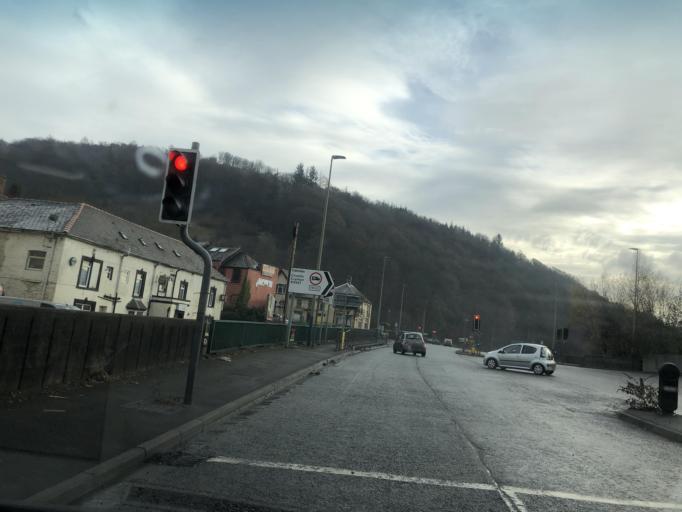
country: GB
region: Wales
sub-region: Caerphilly County Borough
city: Crumlin
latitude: 51.6800
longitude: -3.1393
